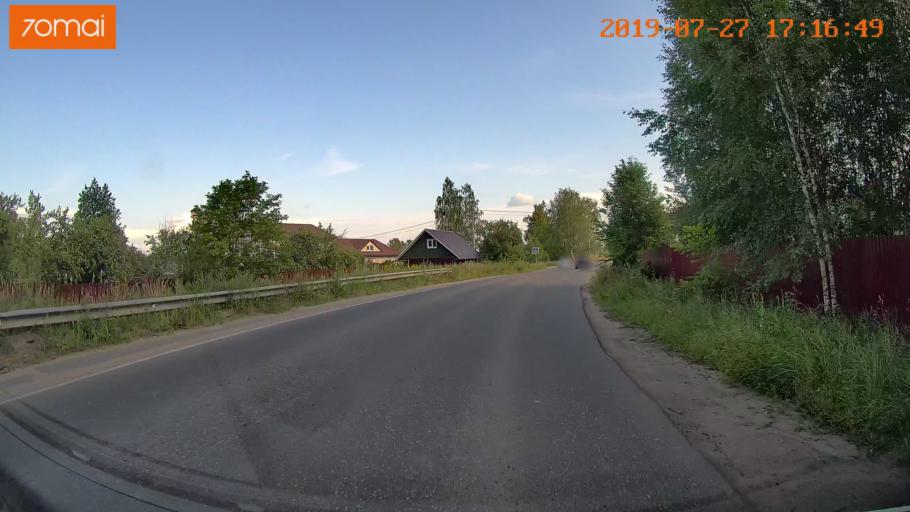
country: RU
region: Ivanovo
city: Novo-Talitsy
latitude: 57.0427
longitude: 40.8900
